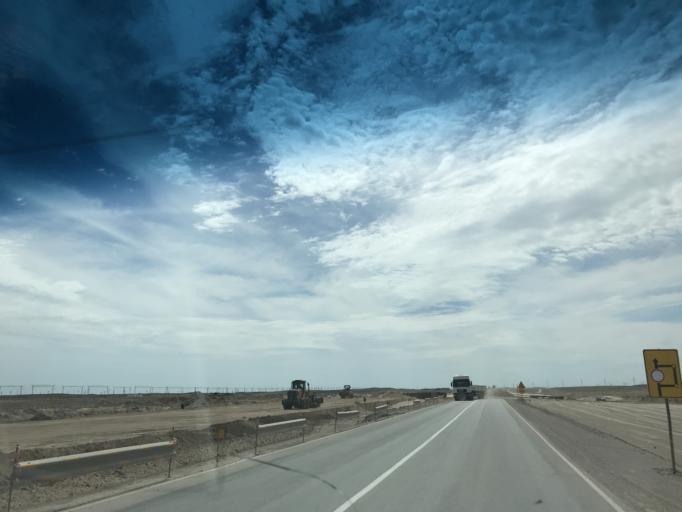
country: KZ
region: Almaty Oblysy
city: Ulken
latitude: 45.2418
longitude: 73.8257
